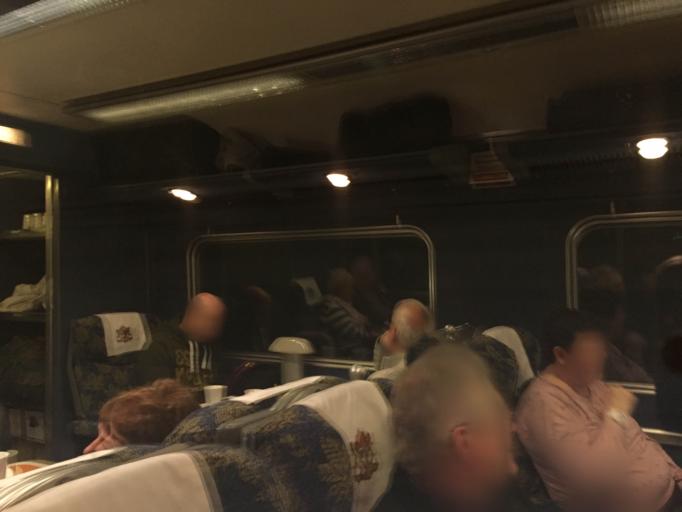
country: GB
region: England
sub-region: Cumbria
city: Sedbergh
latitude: 54.3594
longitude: -2.6106
